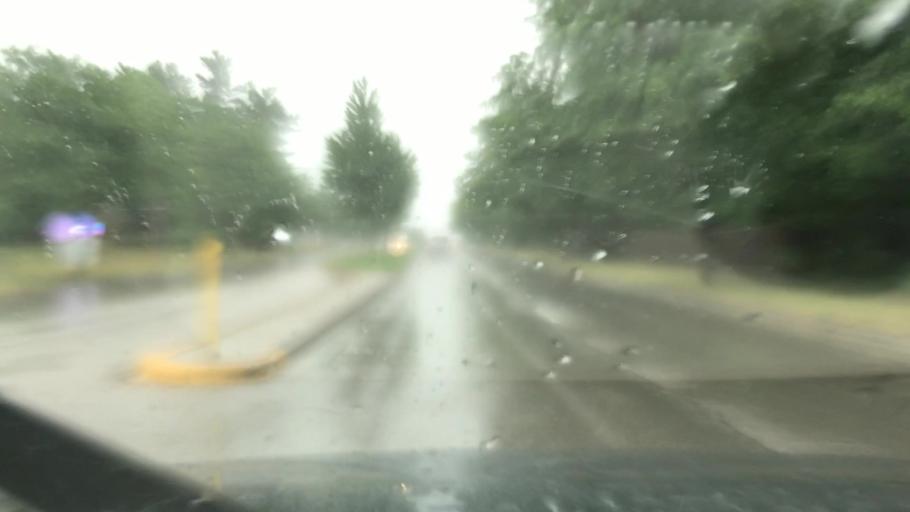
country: US
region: Michigan
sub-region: Kent County
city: Wyoming
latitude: 42.8725
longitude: -85.7236
